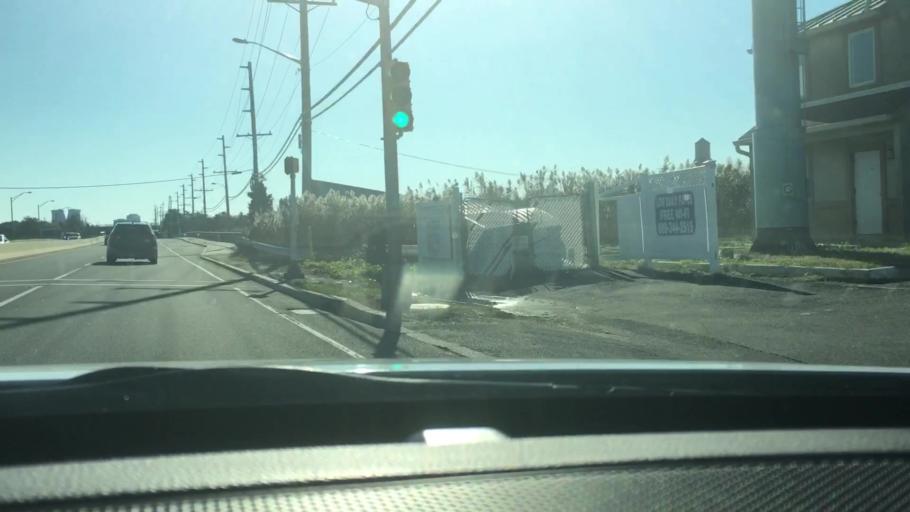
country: US
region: New Jersey
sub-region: Atlantic County
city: Ventnor City
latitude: 39.3712
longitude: -74.4780
